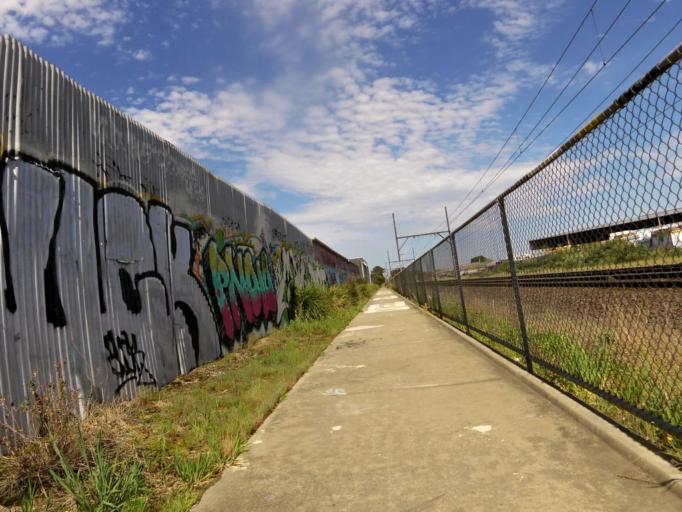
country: AU
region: Victoria
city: Clayton
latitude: -37.9153
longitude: 145.1087
